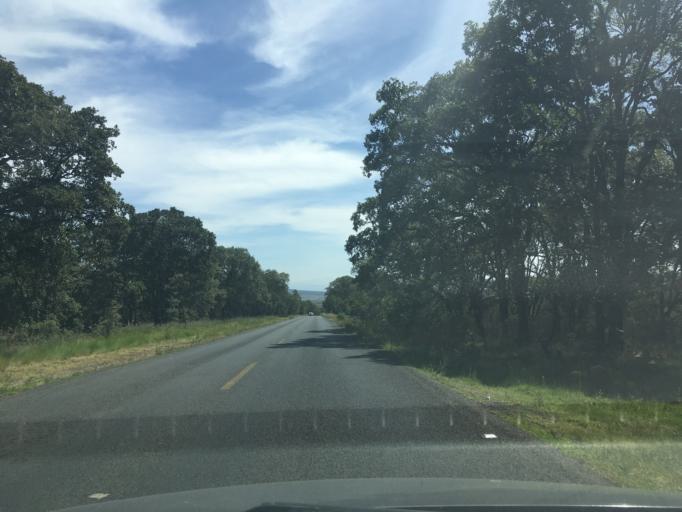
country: MX
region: Queretaro
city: Amealco
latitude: 20.2210
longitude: -100.0987
